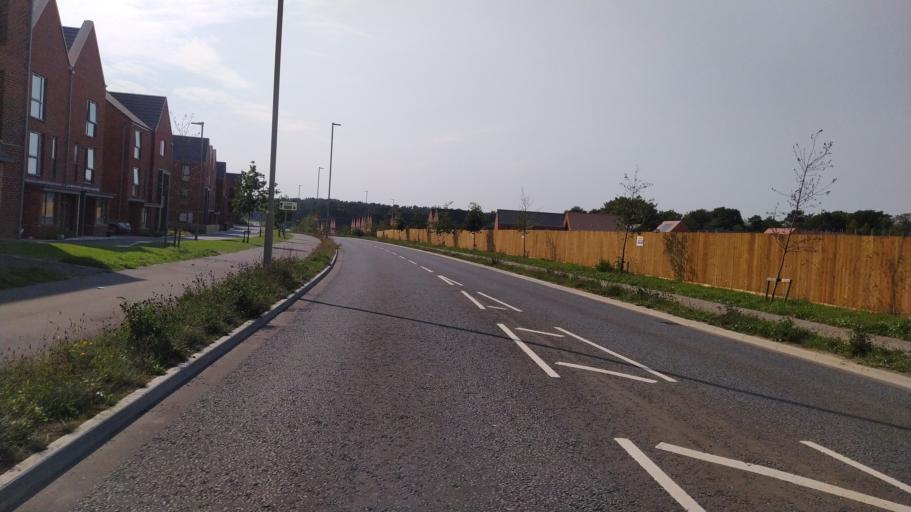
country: GB
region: England
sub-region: Hampshire
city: Bordon
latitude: 51.1236
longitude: -0.8643
